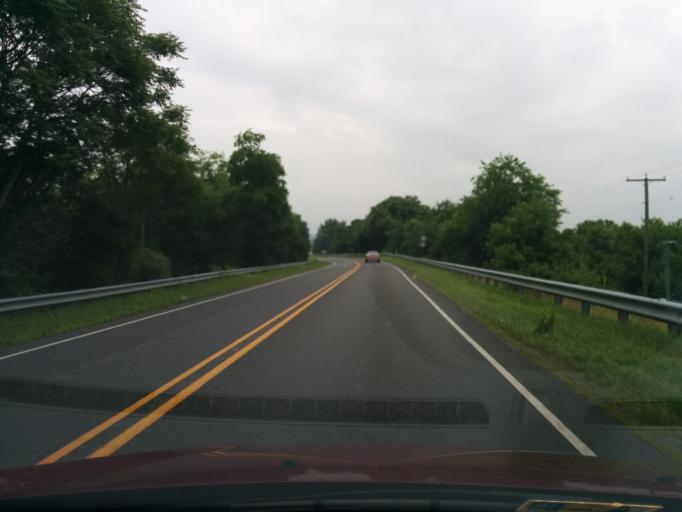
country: US
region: Virginia
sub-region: Rockbridge County
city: East Lexington
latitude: 37.8040
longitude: -79.4188
